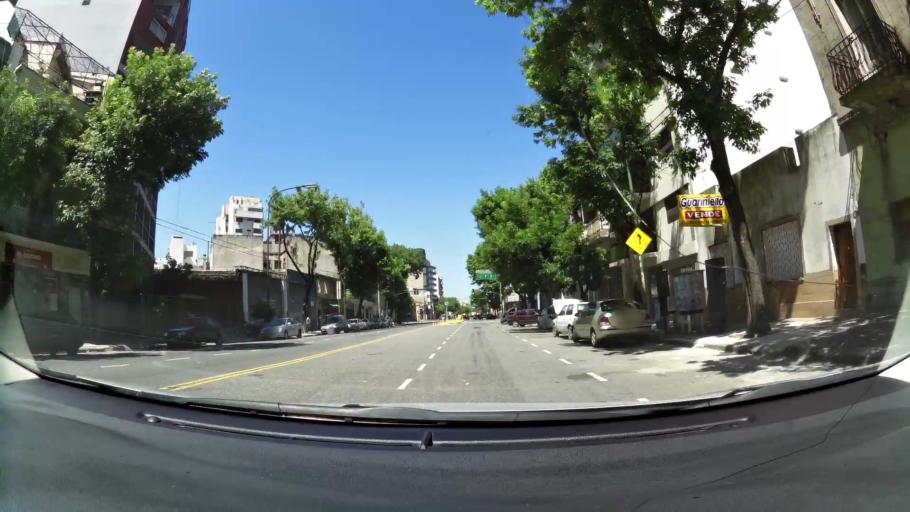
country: AR
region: Buenos Aires F.D.
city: Buenos Aires
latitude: -34.6282
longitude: -58.4046
